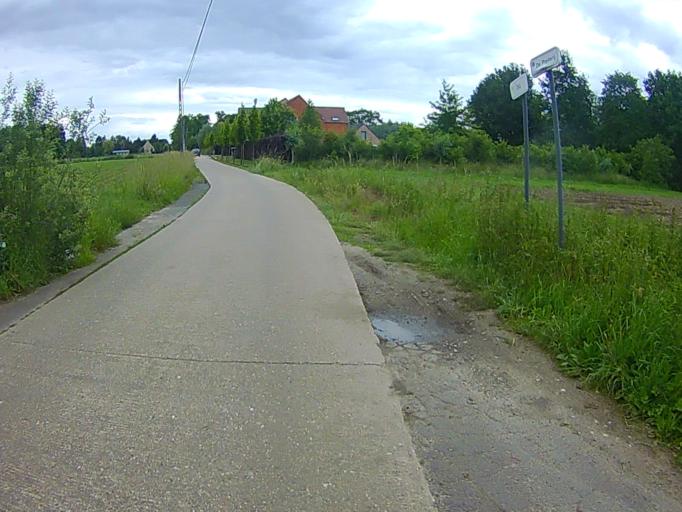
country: BE
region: Flanders
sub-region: Provincie Antwerpen
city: Putte
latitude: 51.0446
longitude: 4.6507
